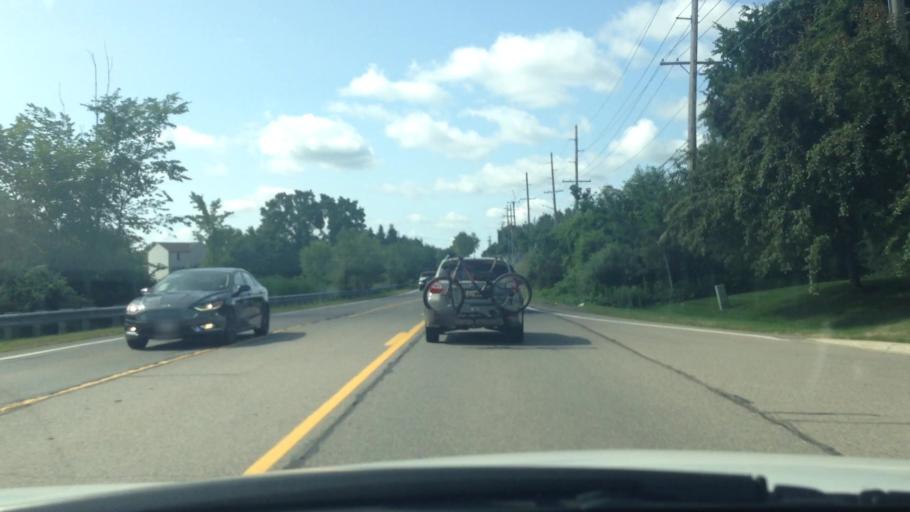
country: US
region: Michigan
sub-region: Oakland County
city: Waterford
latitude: 42.6334
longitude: -83.4428
